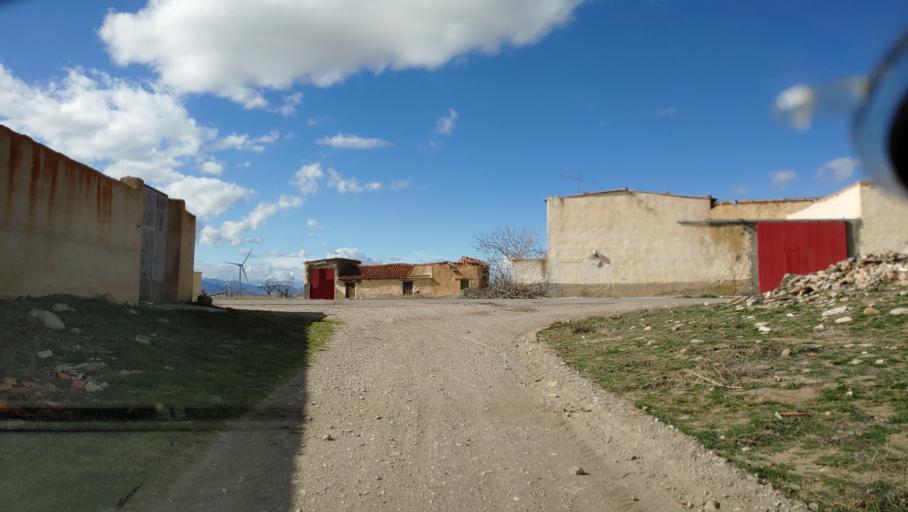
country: ES
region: Andalusia
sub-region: Provincia de Granada
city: Hueneja
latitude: 37.2281
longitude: -2.9621
